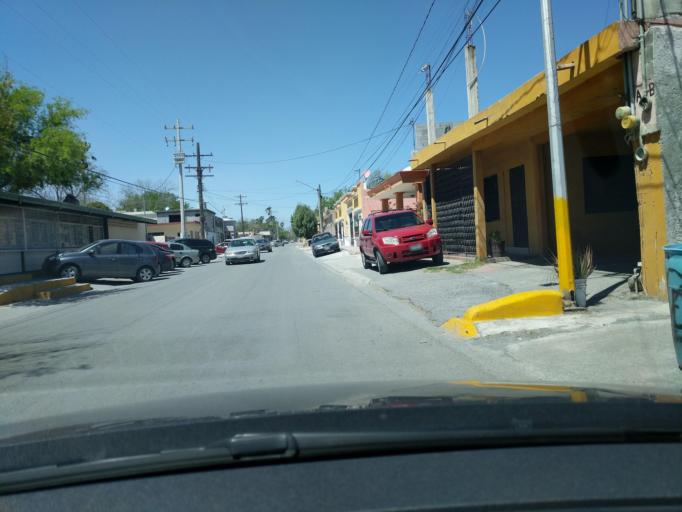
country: MX
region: Nuevo Leon
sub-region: Apodaca
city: Artemio Trevino
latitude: 25.8123
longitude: -100.1470
